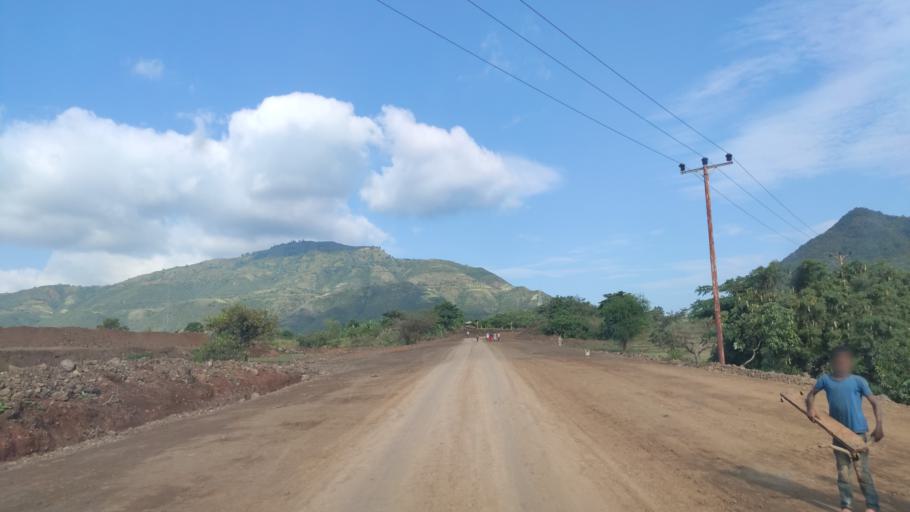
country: ET
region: Southern Nations, Nationalities, and People's Region
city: Arba Minch'
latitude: 6.4270
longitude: 37.3257
